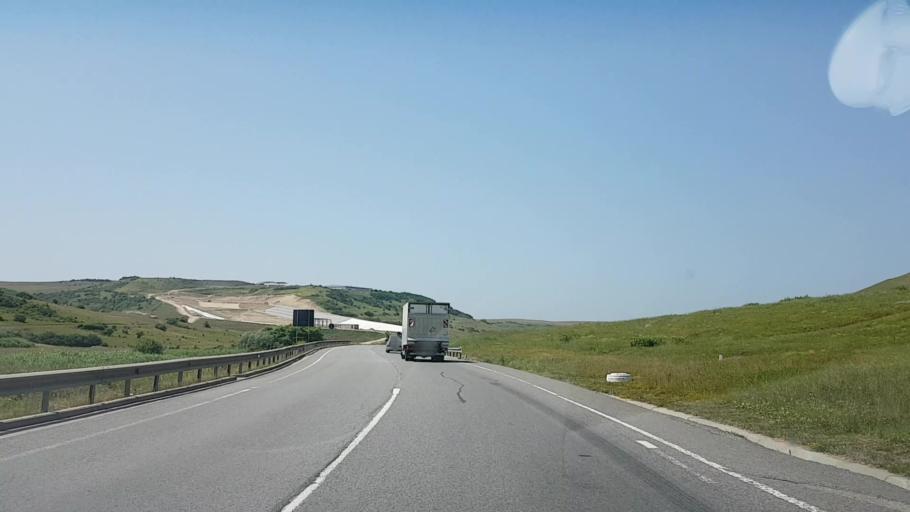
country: RO
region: Cluj
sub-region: Comuna Apahida
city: Dezmir
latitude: 46.7469
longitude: 23.7105
